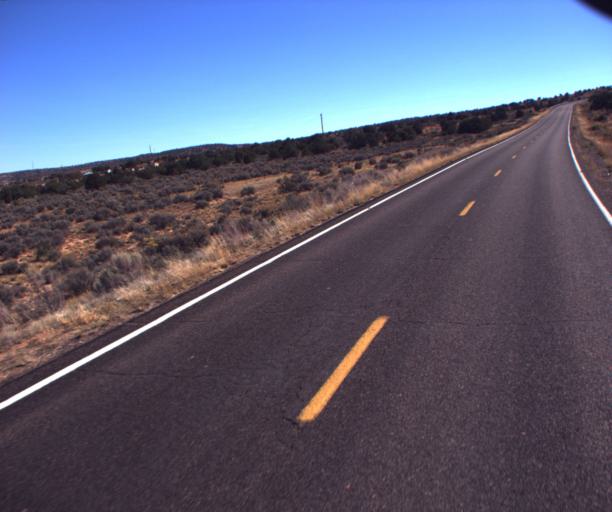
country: US
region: Arizona
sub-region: Navajo County
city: First Mesa
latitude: 35.7473
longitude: -110.1242
